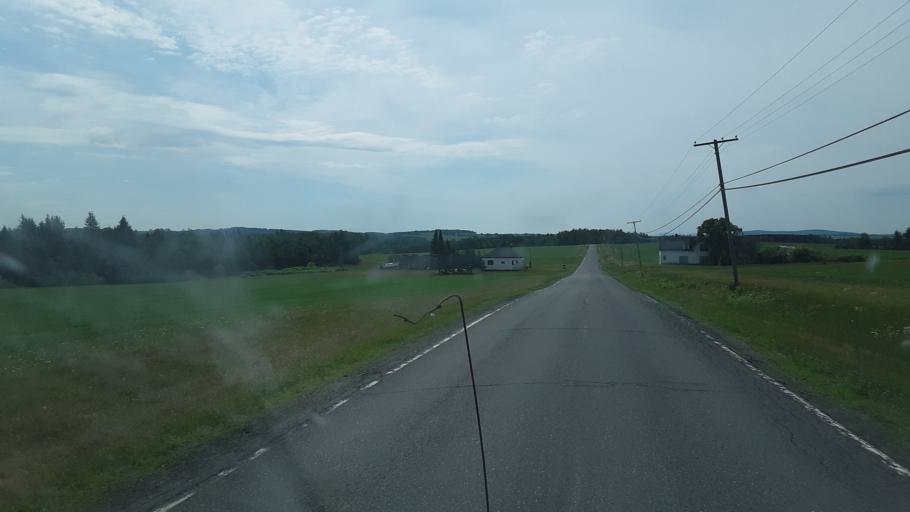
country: US
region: Maine
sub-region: Aroostook County
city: Caribou
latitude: 46.8281
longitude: -68.1763
